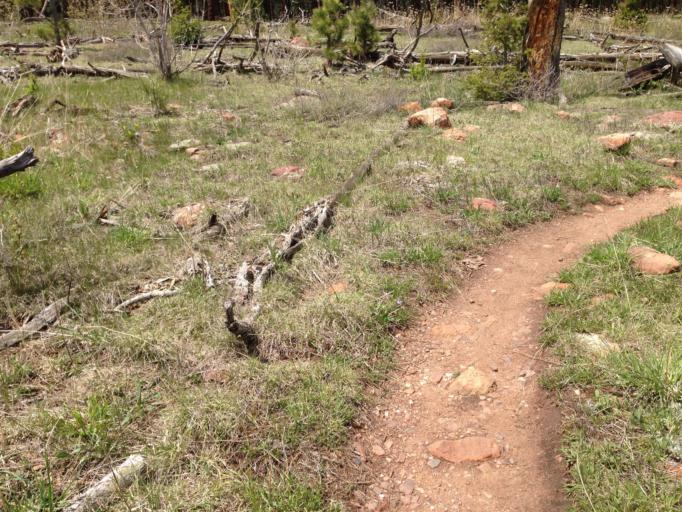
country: US
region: Colorado
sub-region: Boulder County
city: Boulder
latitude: 39.9187
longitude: -105.2689
